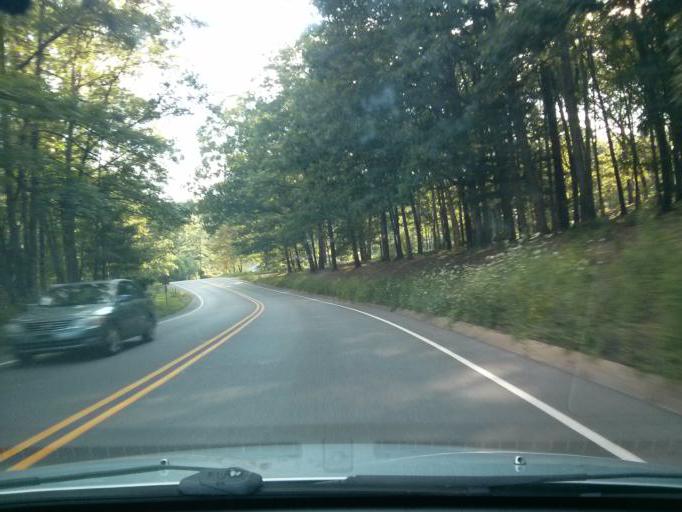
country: US
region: Pennsylvania
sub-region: Centre County
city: Park Forest Village
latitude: 40.8228
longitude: -77.8990
